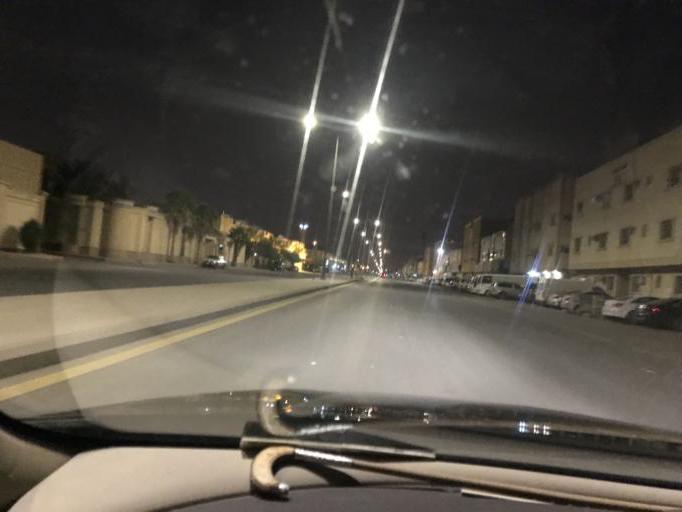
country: SA
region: Ar Riyad
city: Riyadh
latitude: 24.7969
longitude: 46.7067
